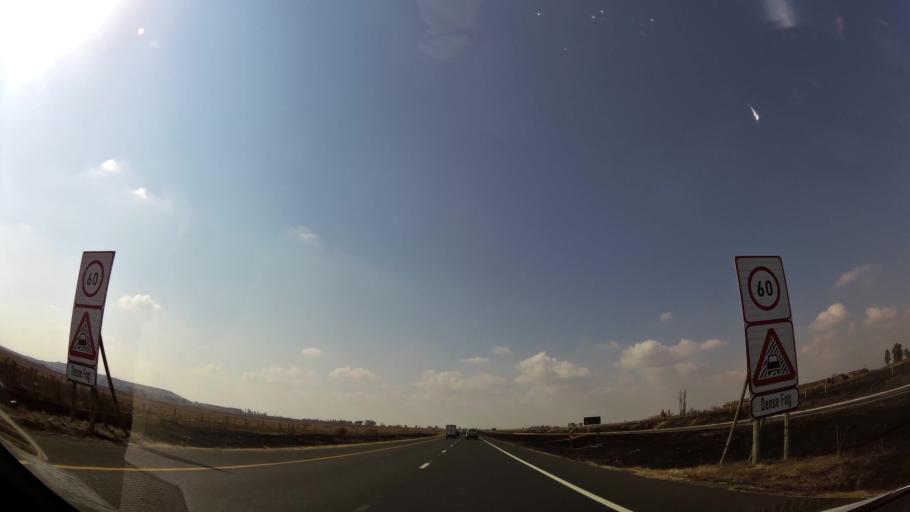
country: ZA
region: Gauteng
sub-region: Ekurhuleni Metropolitan Municipality
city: Springs
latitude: -26.1637
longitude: 28.5030
